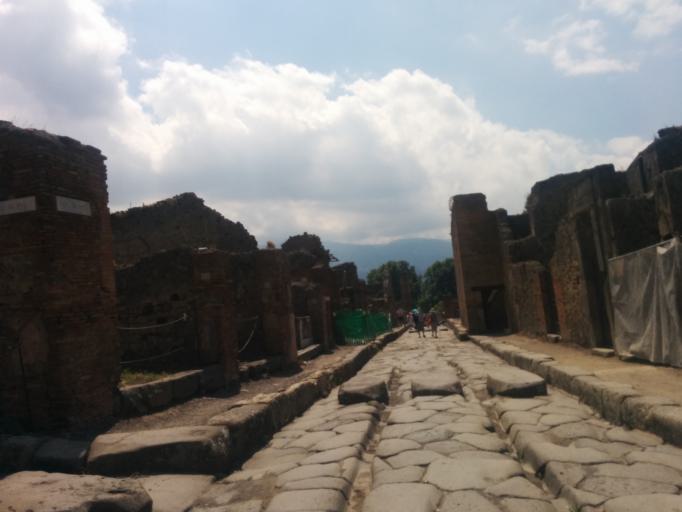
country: IT
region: Campania
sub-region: Provincia di Napoli
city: Pompei
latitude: 40.7505
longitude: 14.4875
